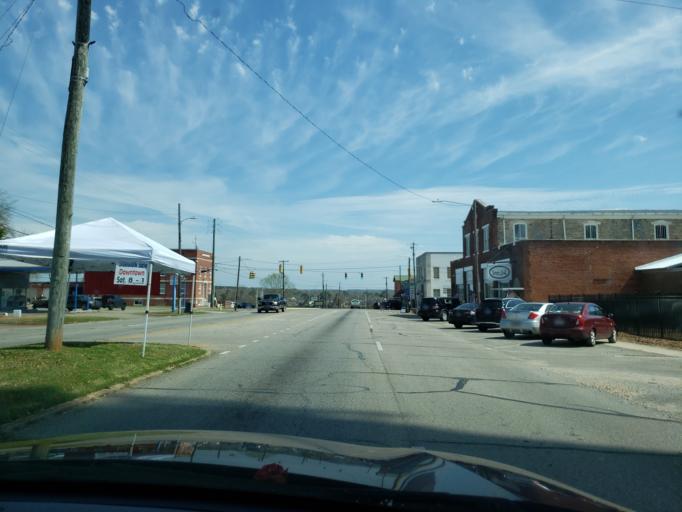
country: US
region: Alabama
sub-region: Elmore County
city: Tallassee
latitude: 32.5359
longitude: -85.8938
